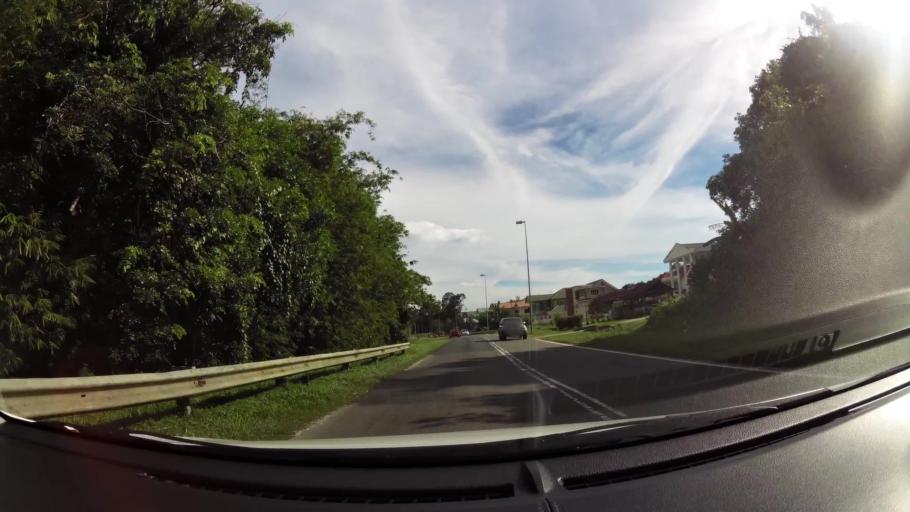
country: BN
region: Brunei and Muara
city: Bandar Seri Begawan
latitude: 4.9831
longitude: 115.0221
